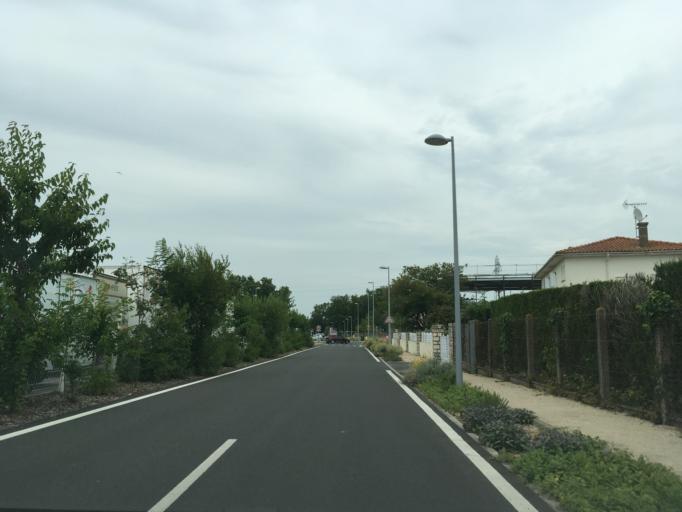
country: FR
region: Poitou-Charentes
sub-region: Departement des Deux-Sevres
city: Bessines
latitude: 46.3056
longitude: -0.4849
